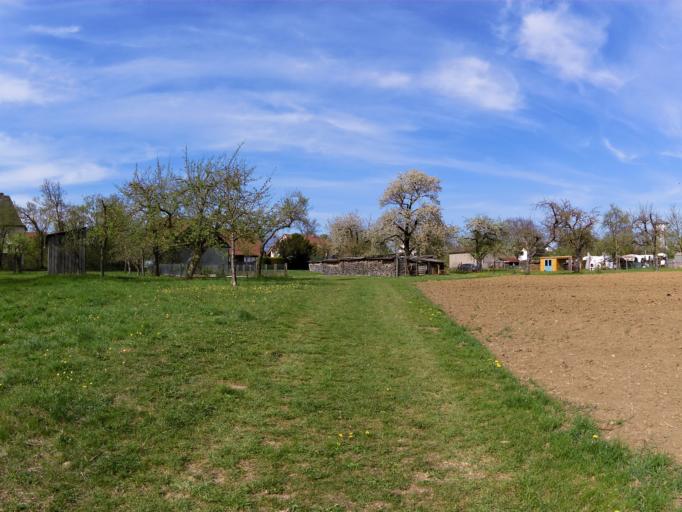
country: DE
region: Bavaria
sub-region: Regierungsbezirk Unterfranken
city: Unterpleichfeld
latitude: 49.8703
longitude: 10.0319
